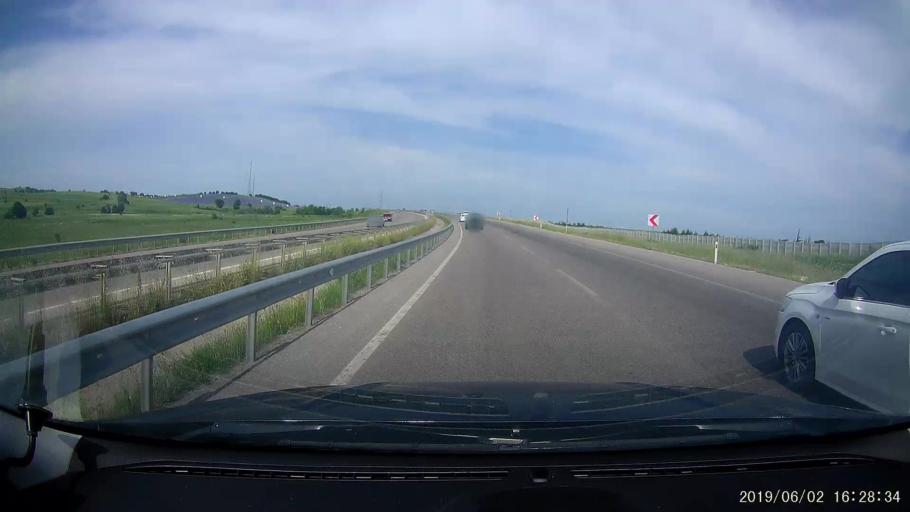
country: TR
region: Samsun
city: Ladik
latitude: 41.0071
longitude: 35.8504
